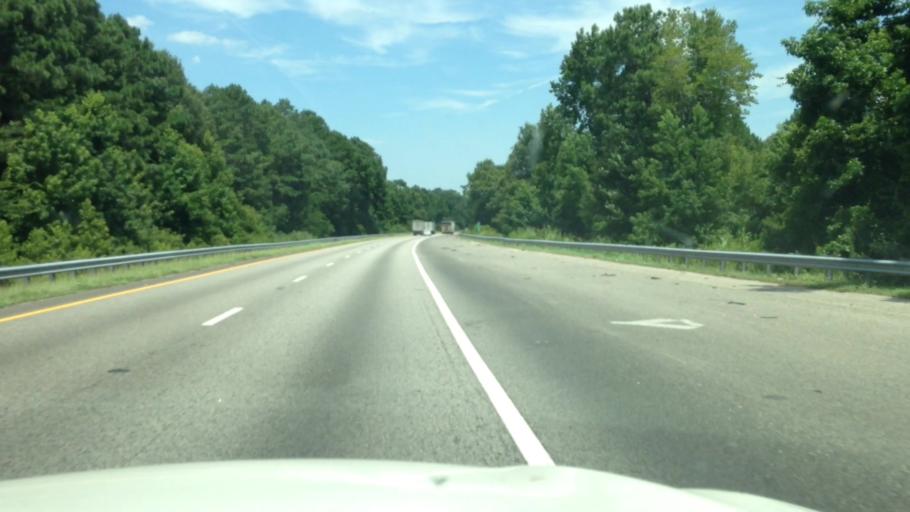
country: US
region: South Carolina
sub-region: Florence County
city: Florence
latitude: 34.2811
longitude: -79.6824
